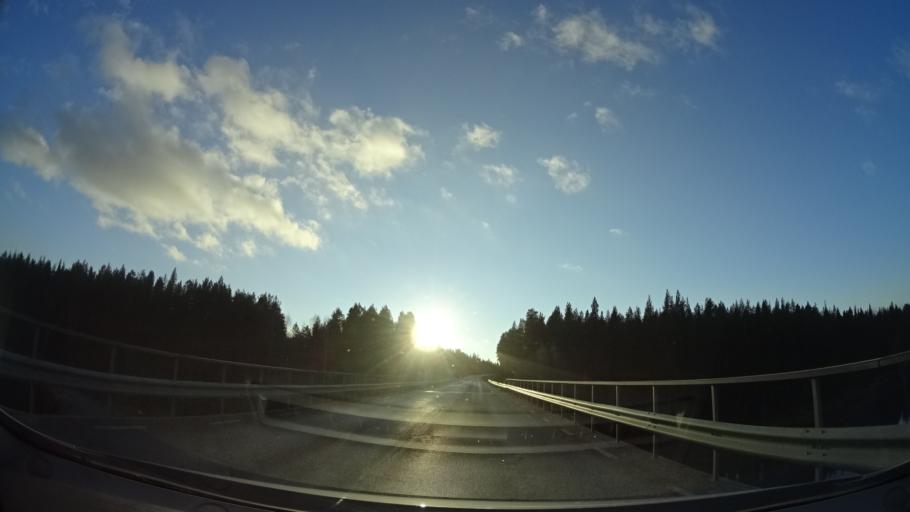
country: SE
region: Vaesterbotten
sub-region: Lycksele Kommun
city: Lycksele
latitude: 64.8231
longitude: 18.7937
